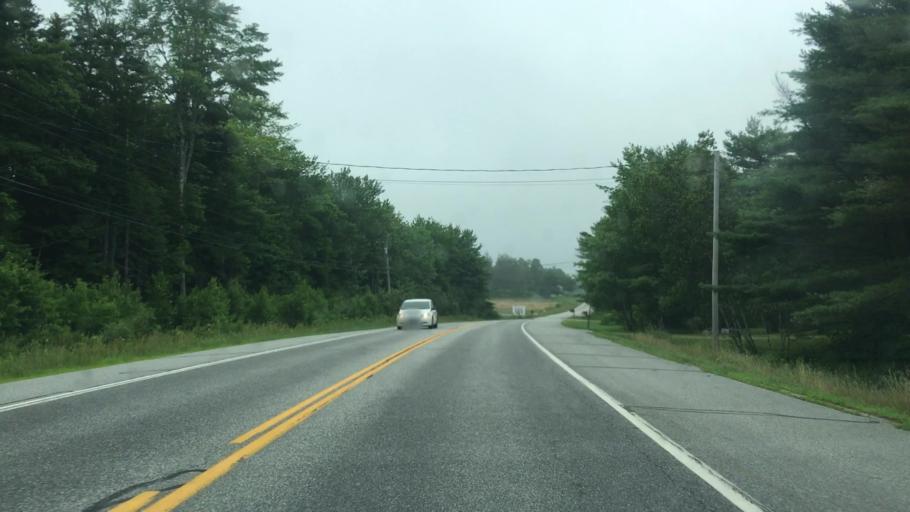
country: US
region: Maine
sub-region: Lincoln County
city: Edgecomb
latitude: 43.9435
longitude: -69.6275
